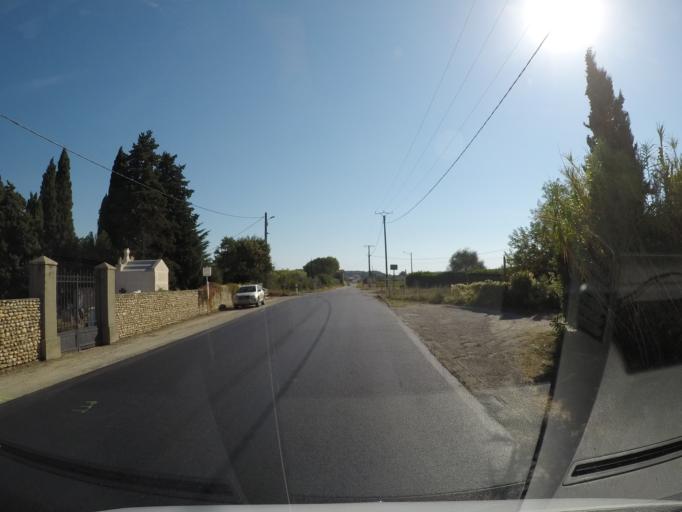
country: FR
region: Languedoc-Roussillon
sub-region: Departement du Gard
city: Ribaute-les-Tavernes
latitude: 44.0239
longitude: 4.0885
